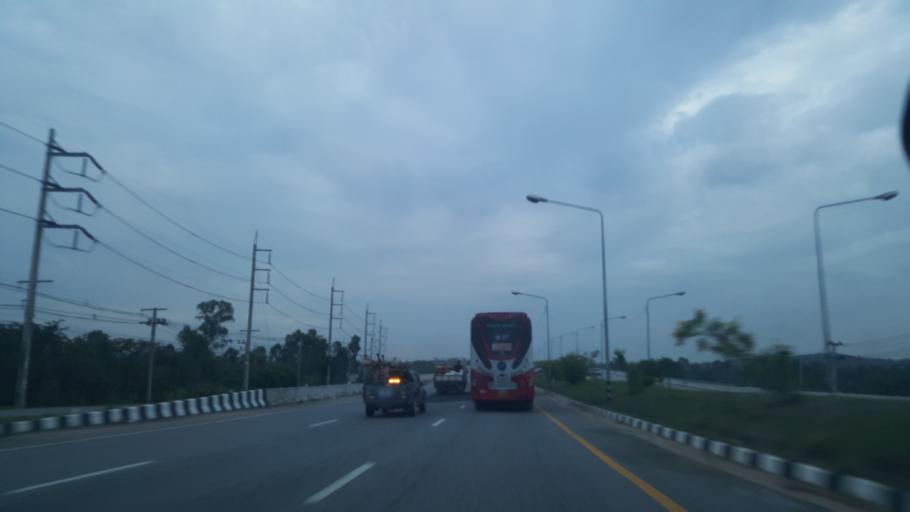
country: TH
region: Chon Buri
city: Phatthaya
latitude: 12.9114
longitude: 101.0297
